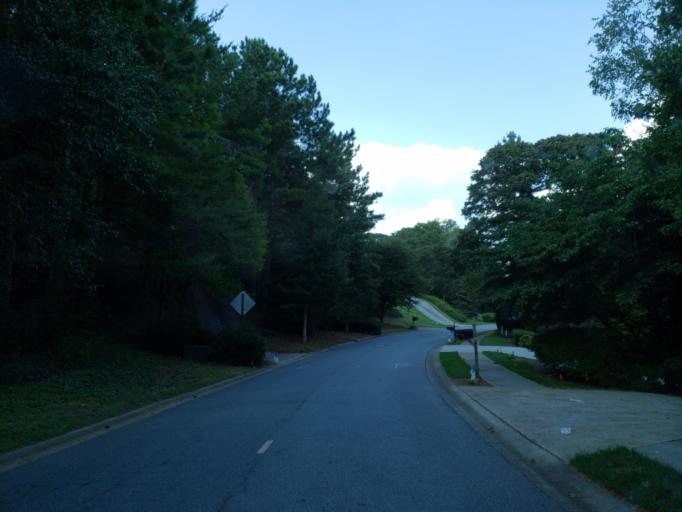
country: US
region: Georgia
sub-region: Cherokee County
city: Woodstock
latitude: 34.0538
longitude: -84.4504
